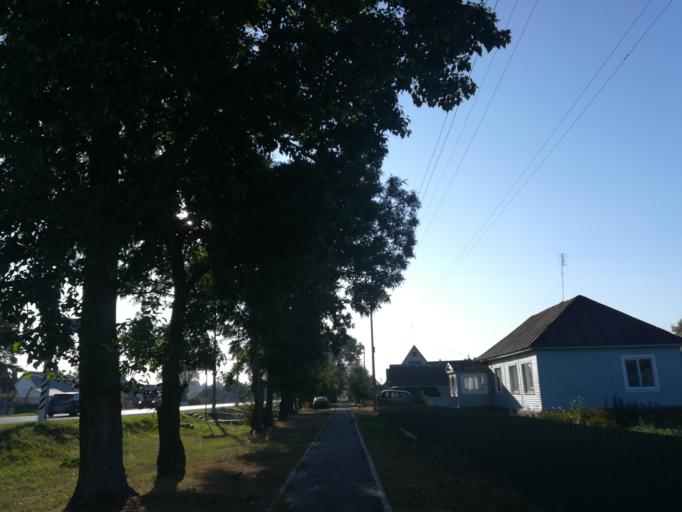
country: RU
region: Brjansk
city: Karachev
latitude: 53.1278
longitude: 34.9382
